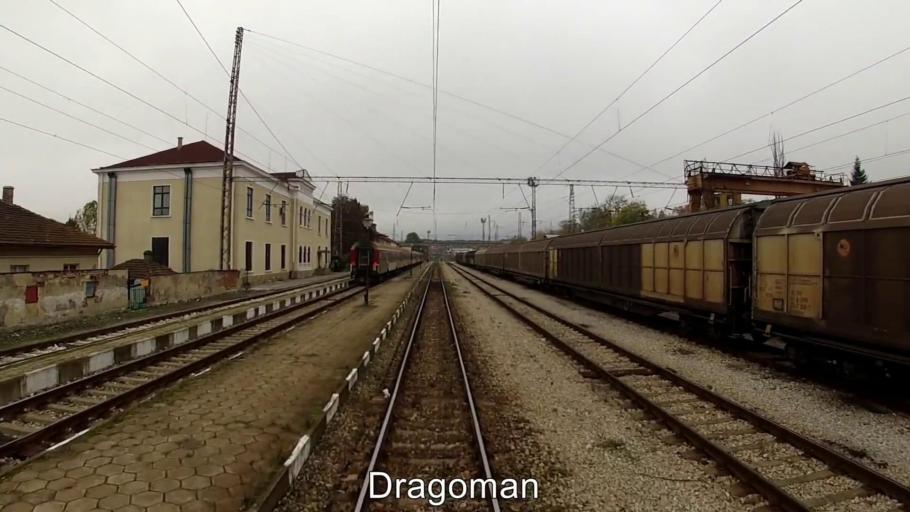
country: BG
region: Sofiya
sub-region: Obshtina Dragoman
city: Dragoman
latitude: 42.9256
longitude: 22.9329
